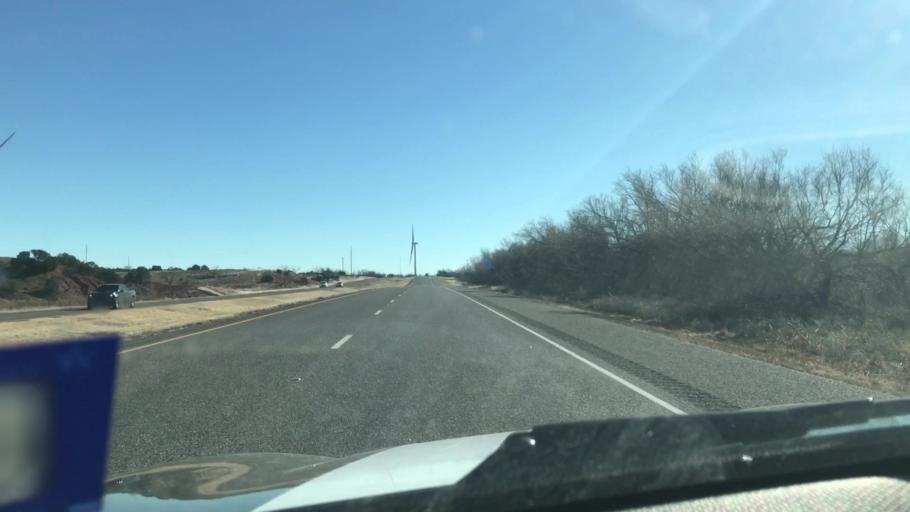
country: US
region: Texas
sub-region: Scurry County
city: Snyder
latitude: 32.8926
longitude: -101.0547
